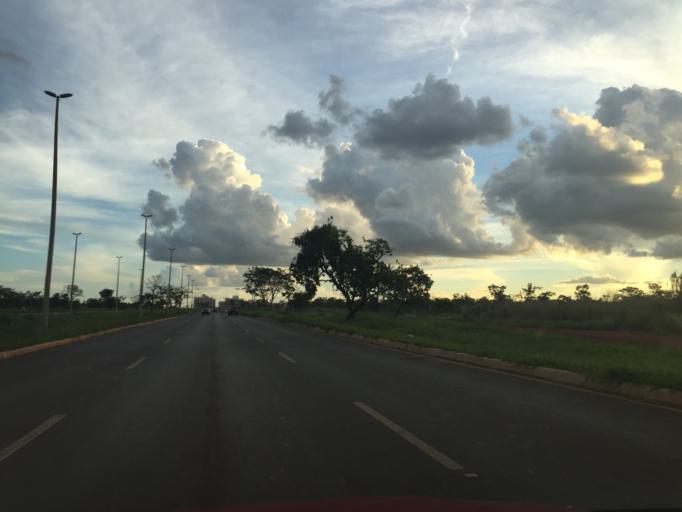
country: BR
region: Federal District
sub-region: Brasilia
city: Brasilia
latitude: -15.8046
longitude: -47.9920
